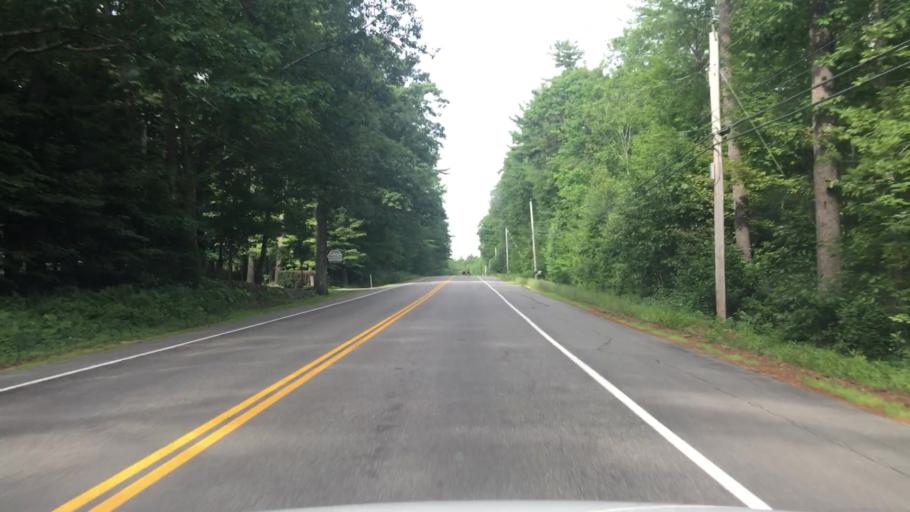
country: US
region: New Hampshire
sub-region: Carroll County
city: Sandwich
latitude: 43.8219
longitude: -71.3442
